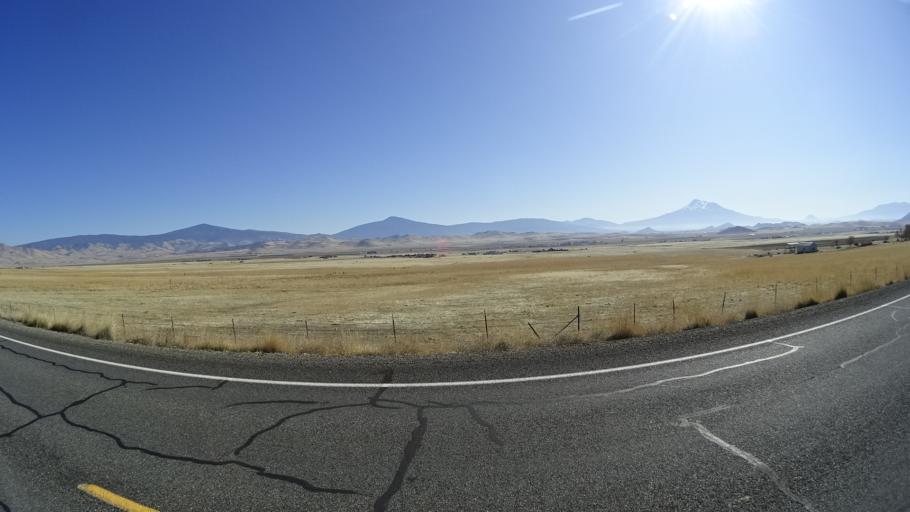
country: US
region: California
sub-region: Siskiyou County
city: Montague
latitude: 41.7899
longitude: -122.5152
